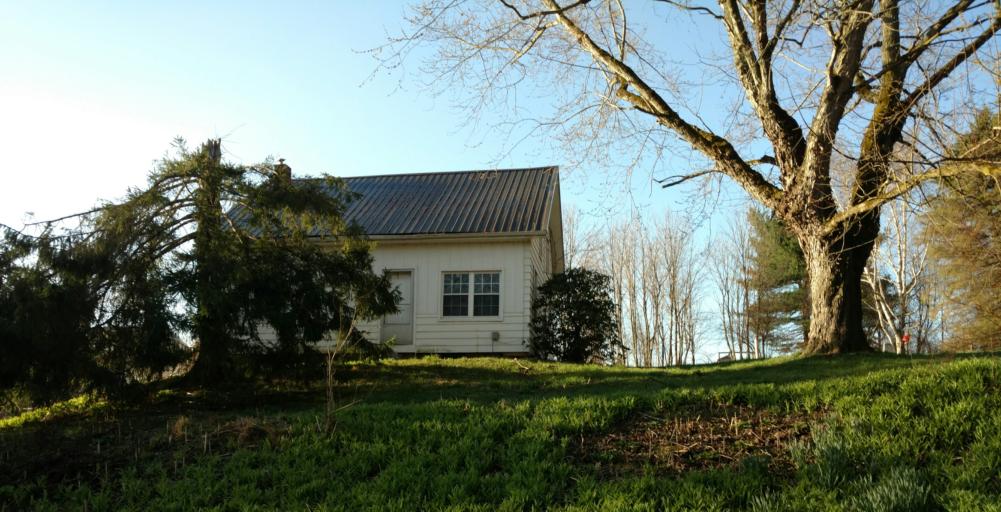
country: US
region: Ohio
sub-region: Richland County
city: Lexington
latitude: 40.5719
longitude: -82.6301
